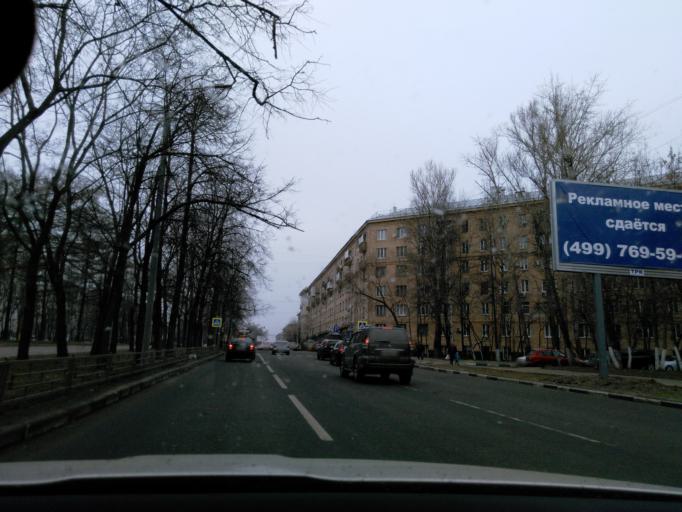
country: RU
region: Moskovskaya
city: Leninskiye Gory
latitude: 55.6931
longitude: 37.5598
